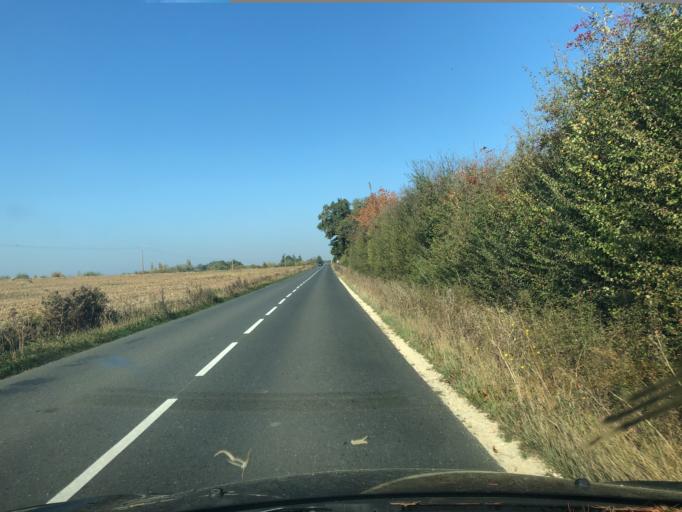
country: FR
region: Centre
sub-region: Departement d'Indre-et-Loire
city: Mettray
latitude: 47.4660
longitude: 0.6691
